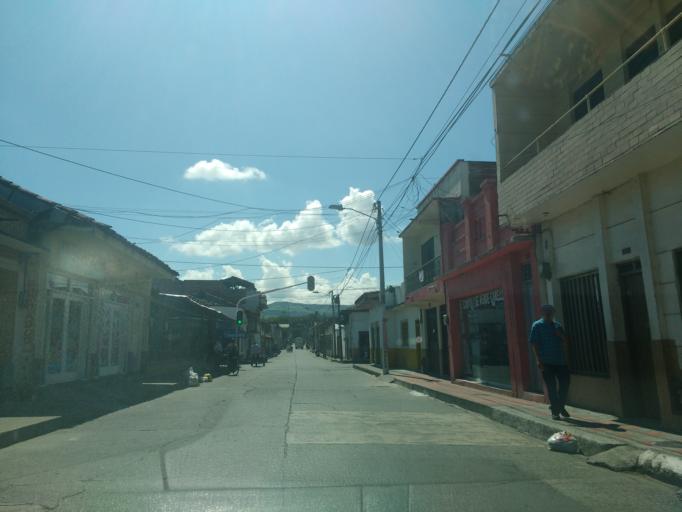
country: CO
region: Valle del Cauca
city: Cartago
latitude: 4.7496
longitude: -75.9058
